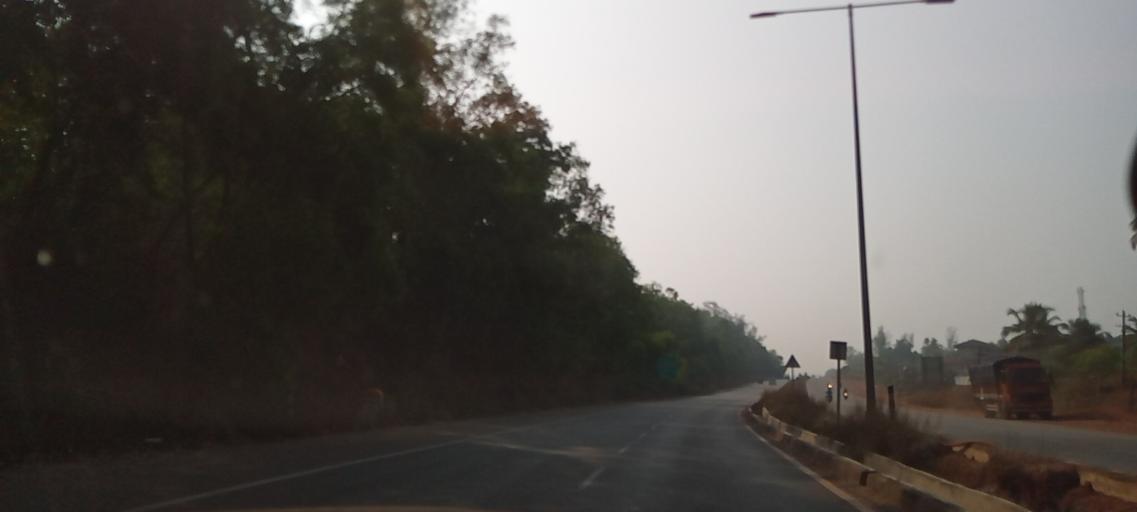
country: IN
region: Karnataka
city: Gangolli
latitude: 13.6767
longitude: 74.6996
